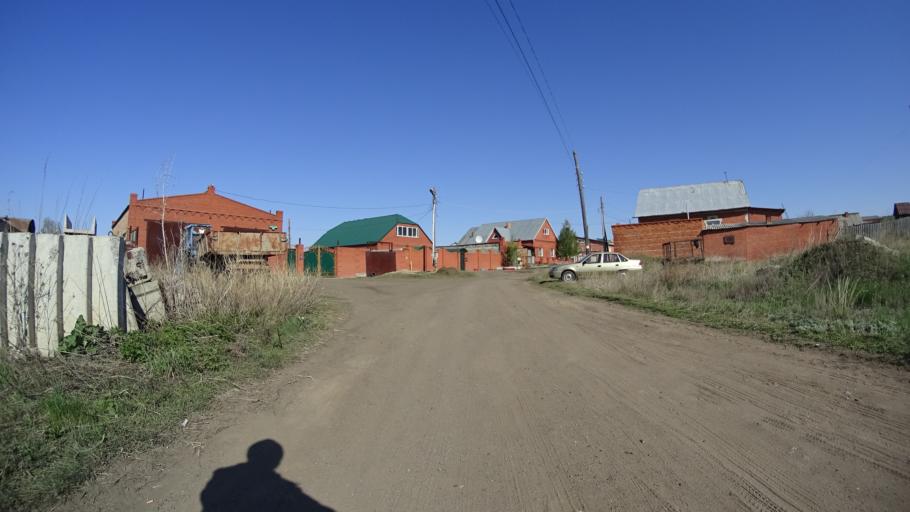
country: RU
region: Chelyabinsk
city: Troitsk
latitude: 54.0965
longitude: 61.5972
